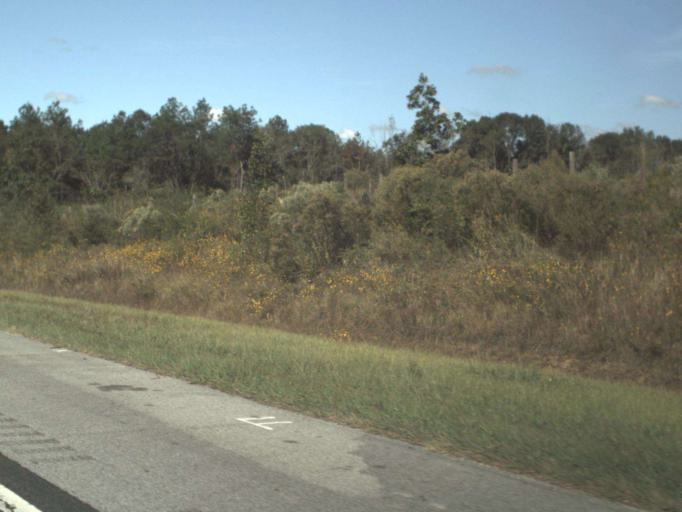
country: US
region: Florida
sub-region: Washington County
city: Chipley
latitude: 30.7513
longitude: -85.5737
